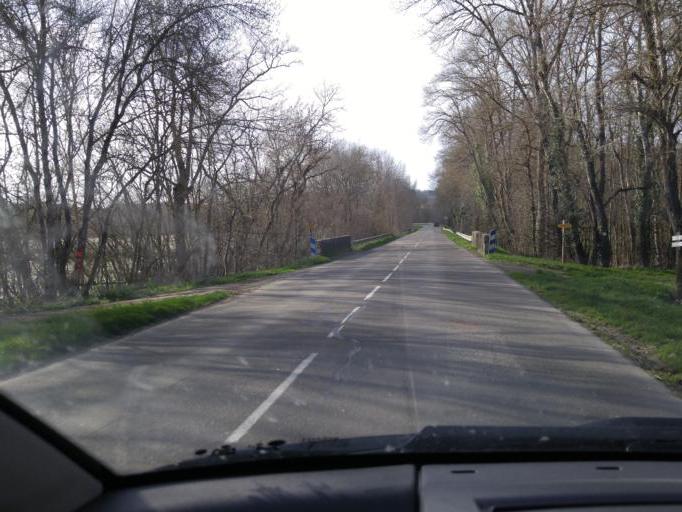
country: FR
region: Midi-Pyrenees
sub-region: Departement du Gers
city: Lectoure
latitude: 43.9343
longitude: 0.6094
